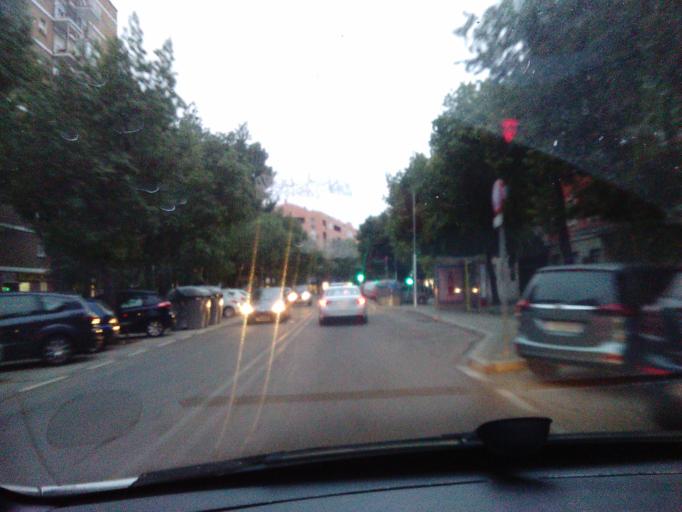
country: ES
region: Andalusia
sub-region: Provincia de Sevilla
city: Sevilla
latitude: 37.3720
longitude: -5.9804
